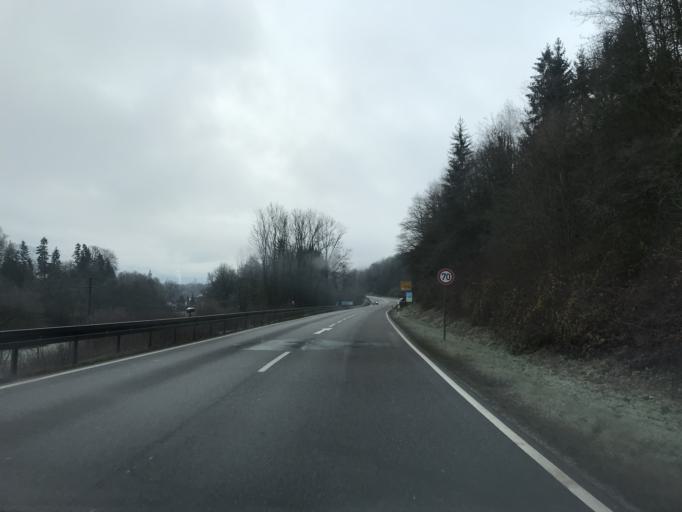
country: DE
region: Baden-Wuerttemberg
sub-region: Freiburg Region
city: Wehr
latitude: 47.6386
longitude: 7.8951
